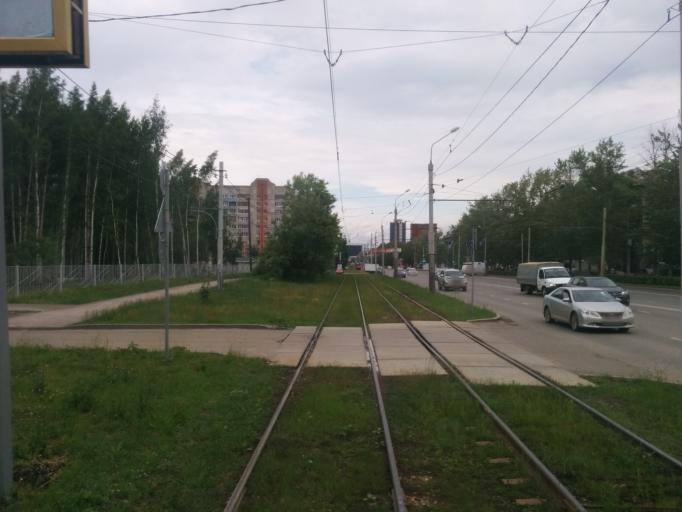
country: RU
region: Perm
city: Perm
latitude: 57.9959
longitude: 56.2874
